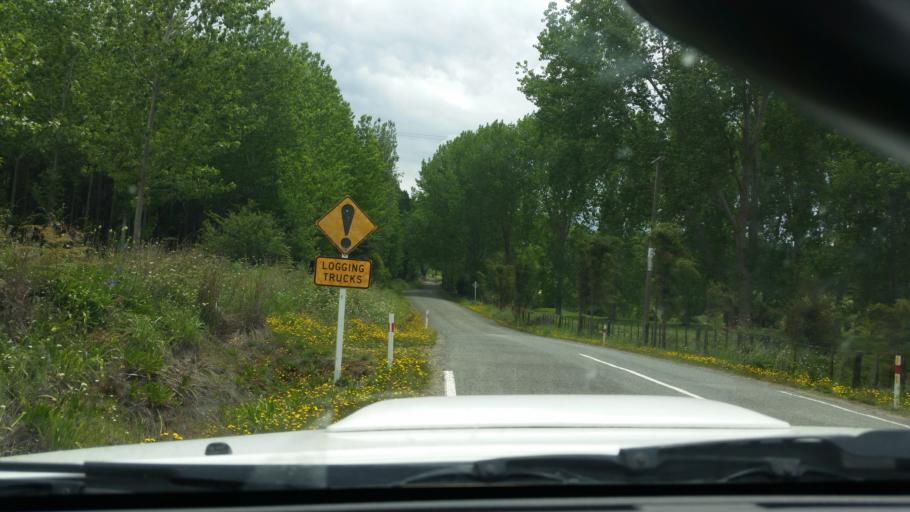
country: NZ
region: Northland
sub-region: Kaipara District
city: Dargaville
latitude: -35.7472
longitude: 173.8770
